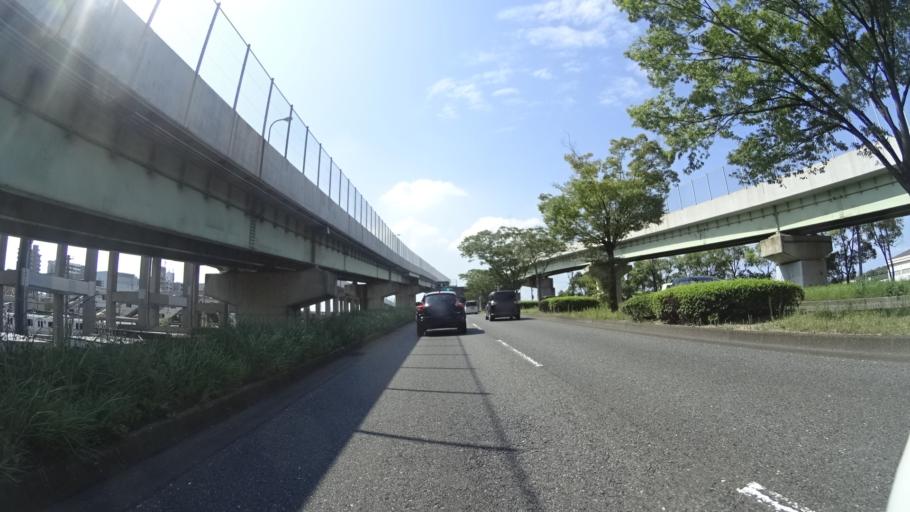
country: JP
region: Fukuoka
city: Kitakyushu
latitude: 33.8890
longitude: 130.8752
